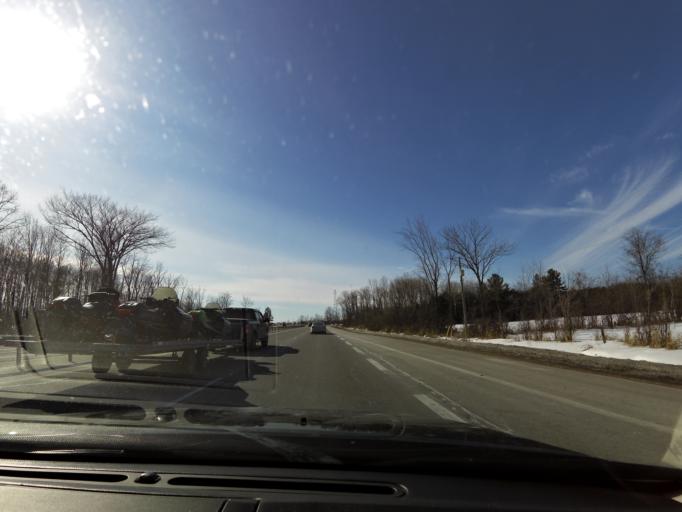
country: CA
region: Ontario
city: Orillia
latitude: 44.4982
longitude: -79.4973
